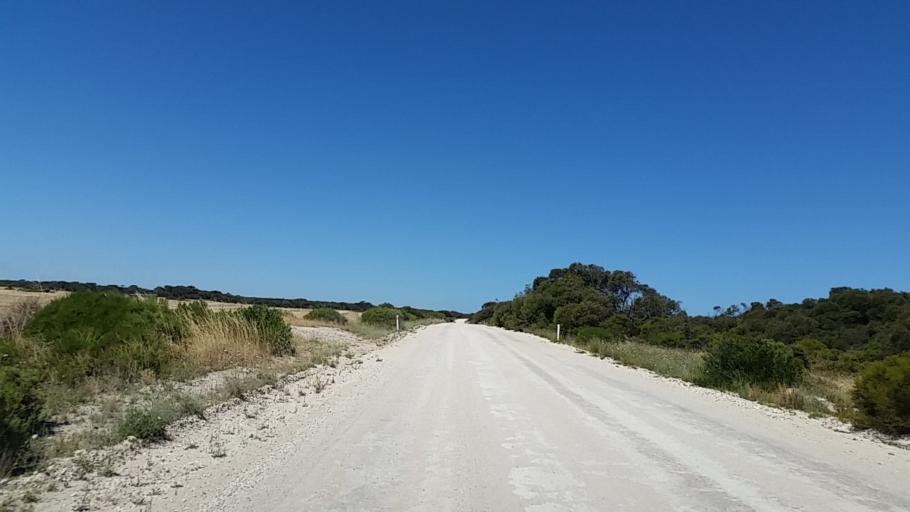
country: AU
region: South Australia
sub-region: Yorke Peninsula
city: Honiton
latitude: -35.2215
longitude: 137.0754
